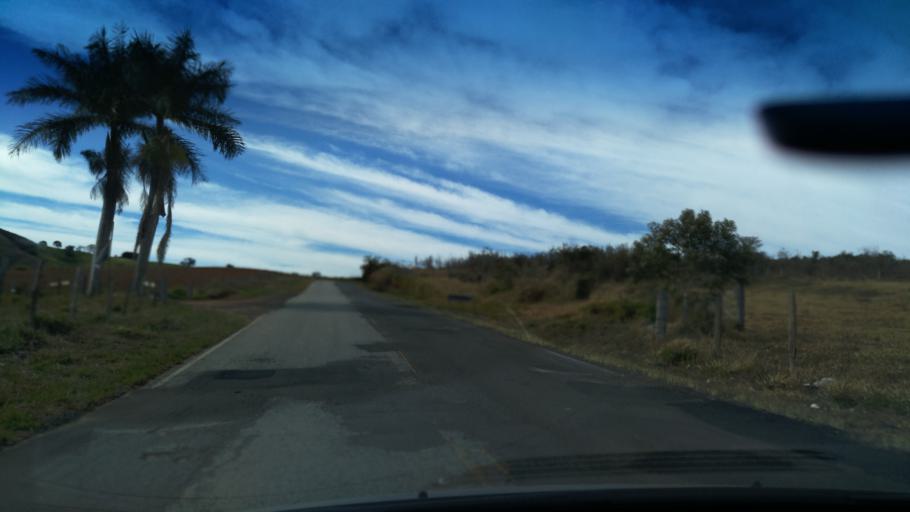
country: BR
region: Minas Gerais
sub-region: Andradas
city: Andradas
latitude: -22.0581
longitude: -46.3948
